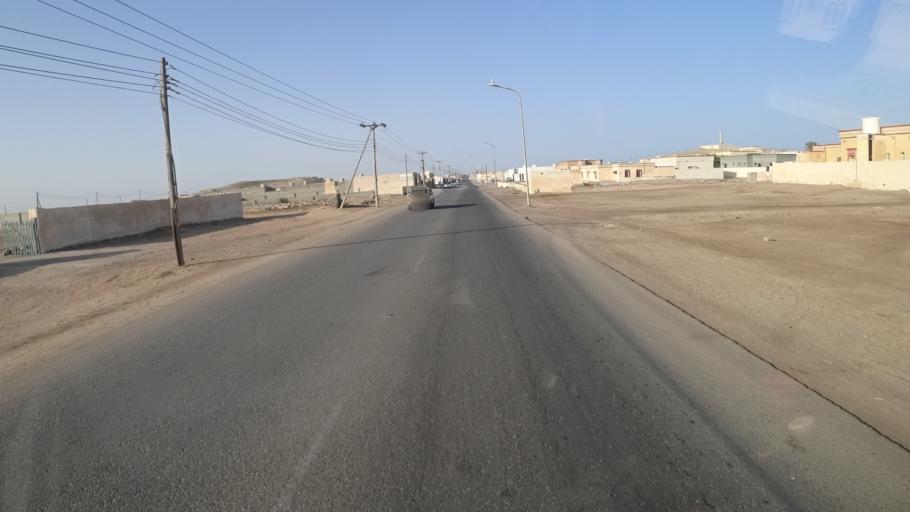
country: OM
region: Ash Sharqiyah
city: Sur
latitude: 22.1754
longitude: 59.7607
